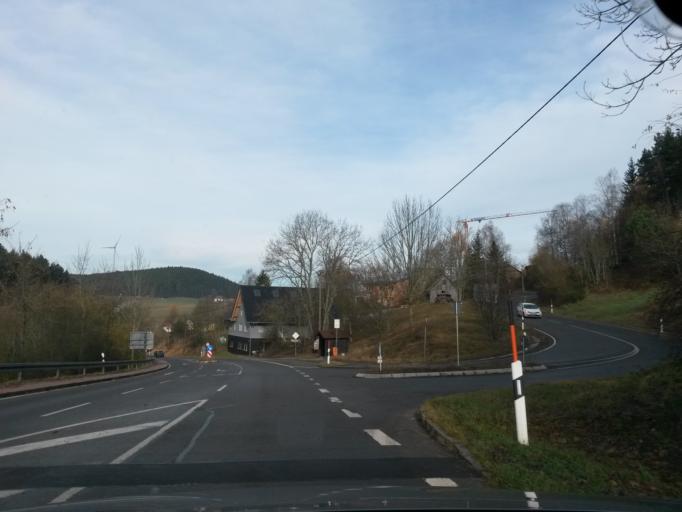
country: DE
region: Baden-Wuerttemberg
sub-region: Freiburg Region
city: Sankt Georgen im Schwarzwald
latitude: 48.1538
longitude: 8.3287
